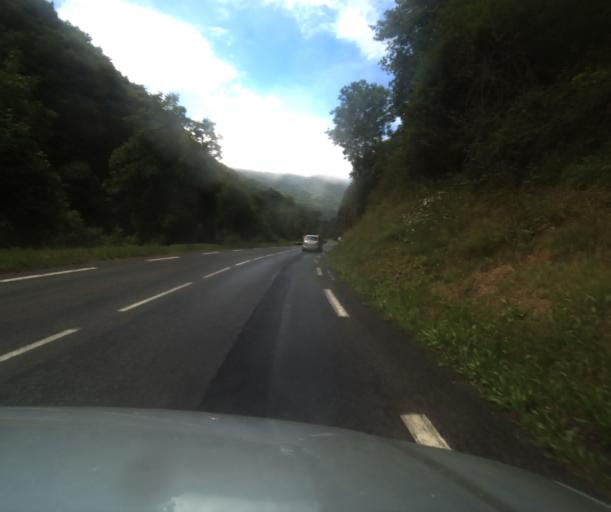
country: FR
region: Midi-Pyrenees
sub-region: Departement des Hautes-Pyrenees
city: Pierrefitte-Nestalas
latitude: 42.9475
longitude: -0.0595
